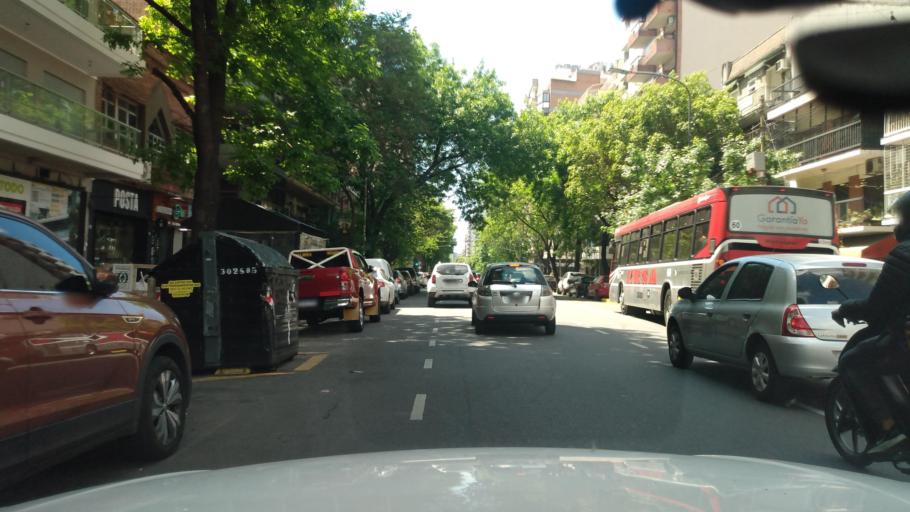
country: AR
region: Buenos Aires F.D.
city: Colegiales
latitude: -34.5752
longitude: -58.4838
